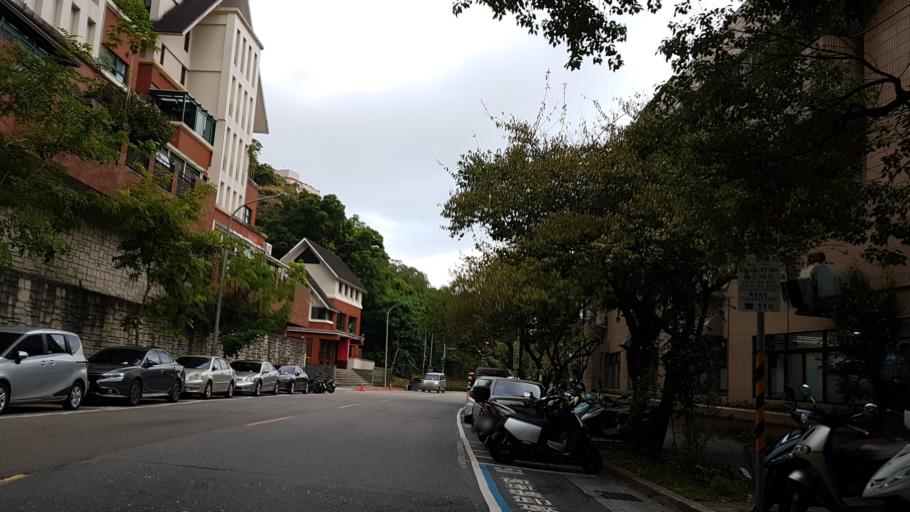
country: TW
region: Taipei
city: Taipei
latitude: 25.0024
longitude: 121.5678
